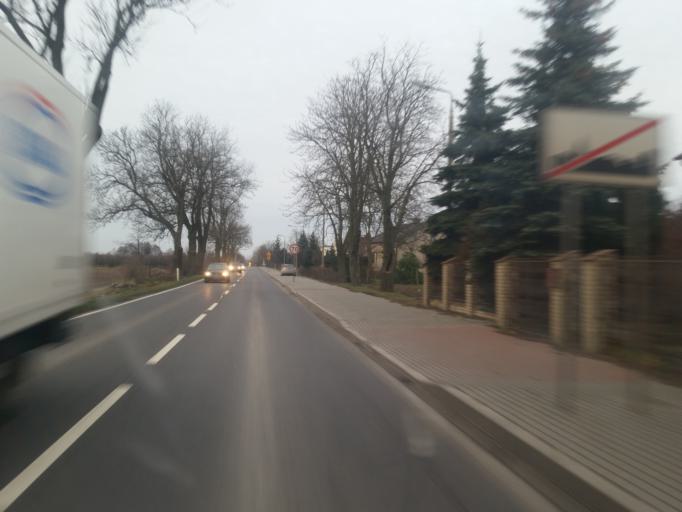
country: PL
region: Kujawsko-Pomorskie
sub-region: Powiat brodnicki
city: Brodnica
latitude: 53.1719
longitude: 19.3870
